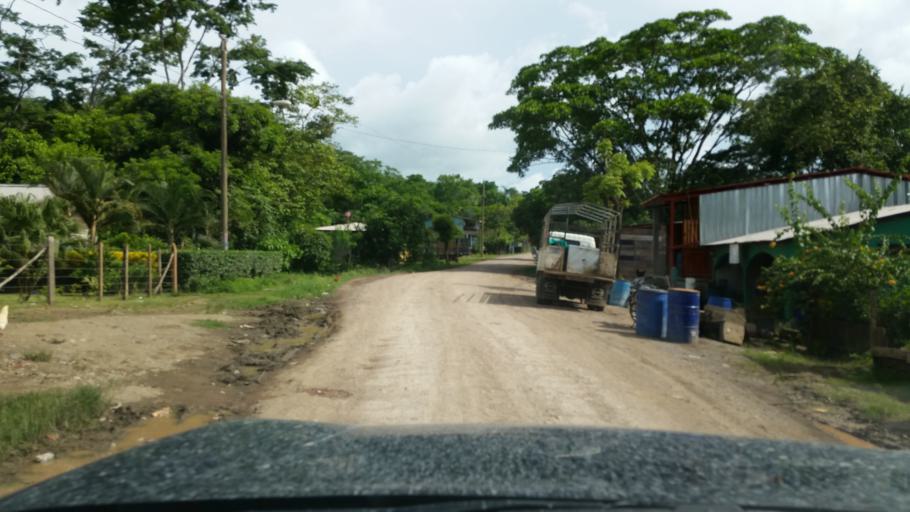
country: NI
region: Atlantico Norte (RAAN)
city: Siuna
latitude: 13.5900
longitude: -84.8122
